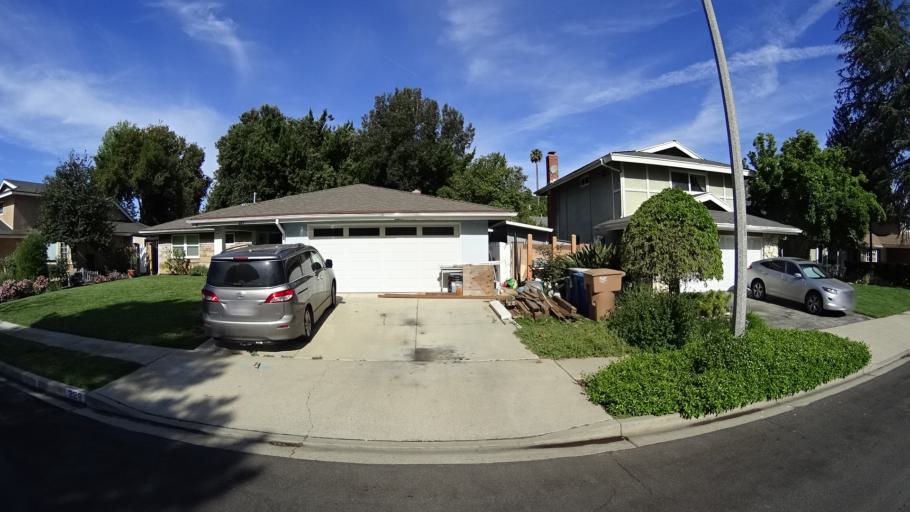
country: US
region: California
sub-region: Ventura County
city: Casa Conejo
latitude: 34.1735
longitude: -118.9559
